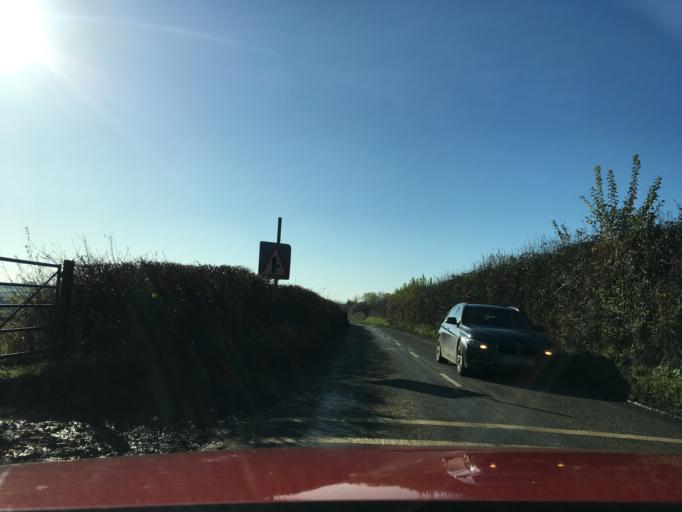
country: GB
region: England
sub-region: Somerset
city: Martock
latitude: 50.9992
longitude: -2.7662
